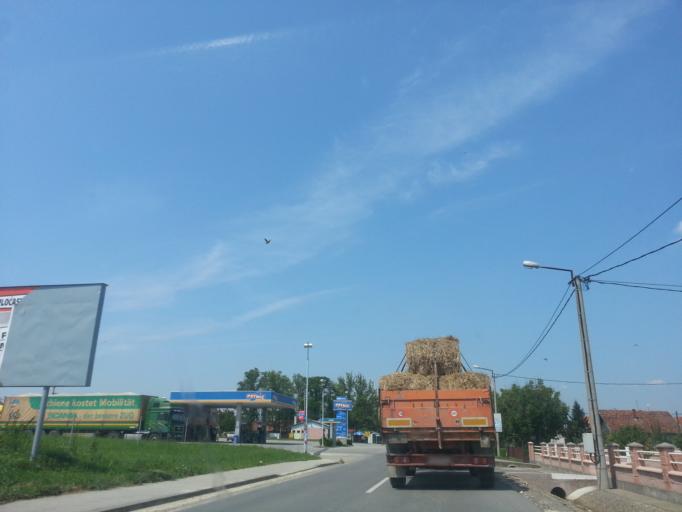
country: BA
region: Brcko
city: Brcko
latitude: 44.8404
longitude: 18.8200
